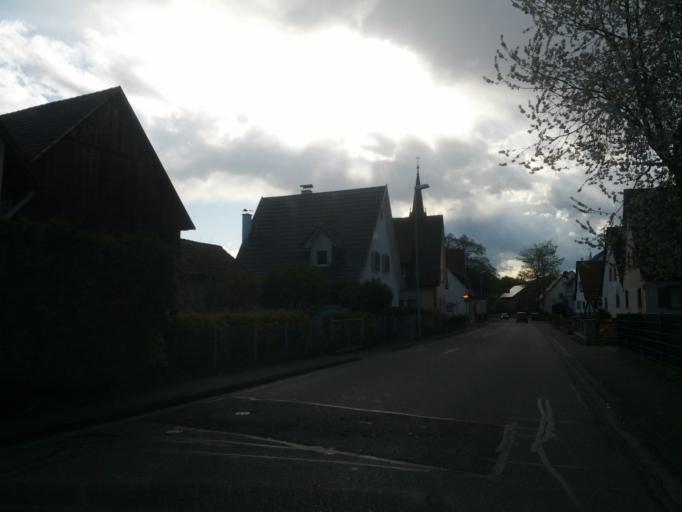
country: DE
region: Baden-Wuerttemberg
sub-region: Freiburg Region
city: Umkirch
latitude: 48.0635
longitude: 7.7839
